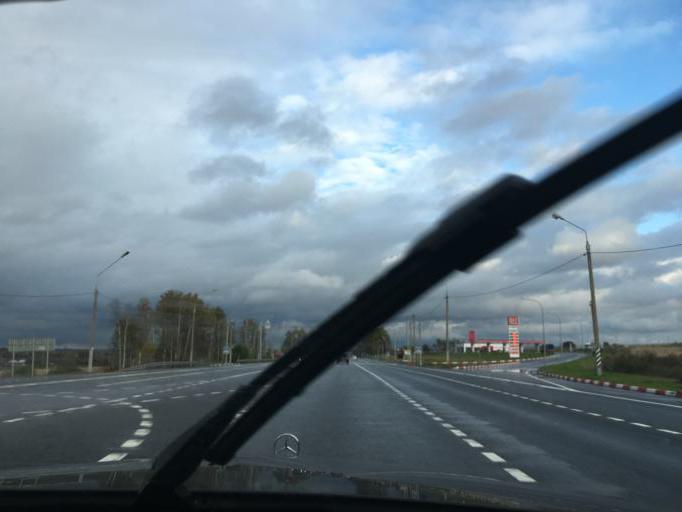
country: RU
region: Smolensk
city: Katyn'
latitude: 54.8505
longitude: 31.8372
